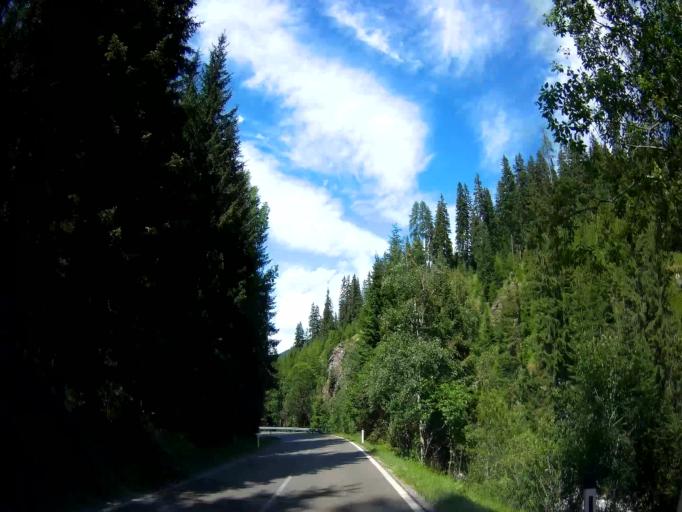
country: AT
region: Styria
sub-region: Politischer Bezirk Murau
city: Stadl an der Mur
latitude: 47.0225
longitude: 14.0061
